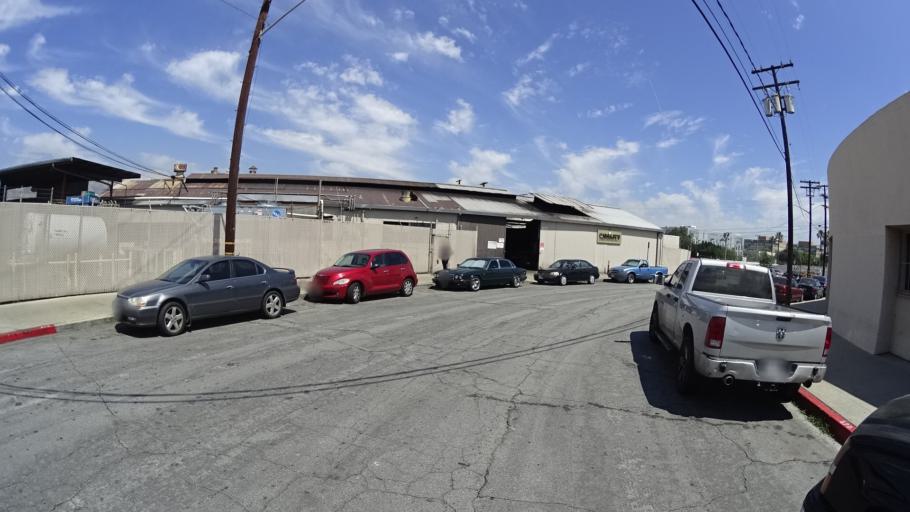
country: US
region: California
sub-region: Los Angeles County
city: North Hollywood
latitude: 34.1971
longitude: -118.3472
